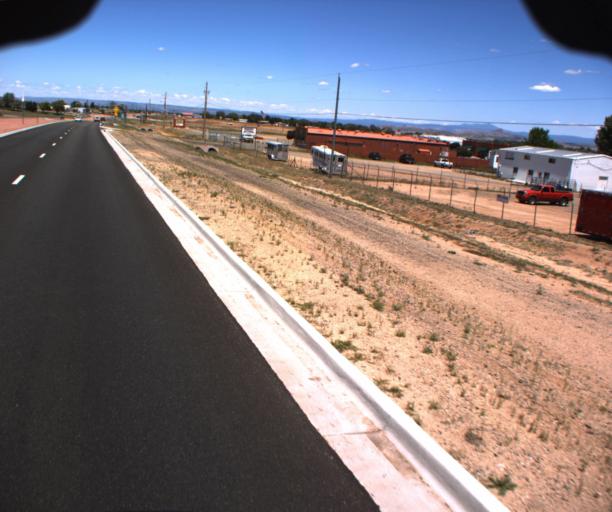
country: US
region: Arizona
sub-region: Yavapai County
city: Chino Valley
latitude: 34.7114
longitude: -112.4521
